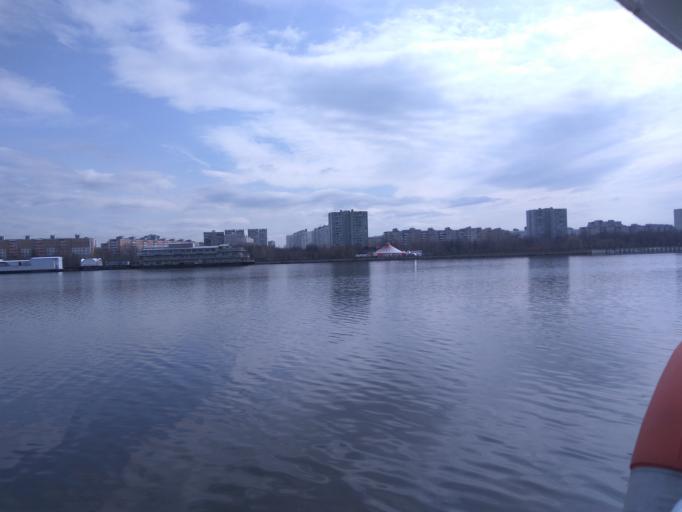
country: RU
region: Moscow
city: Kolomenskoye
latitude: 55.6862
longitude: 37.7097
